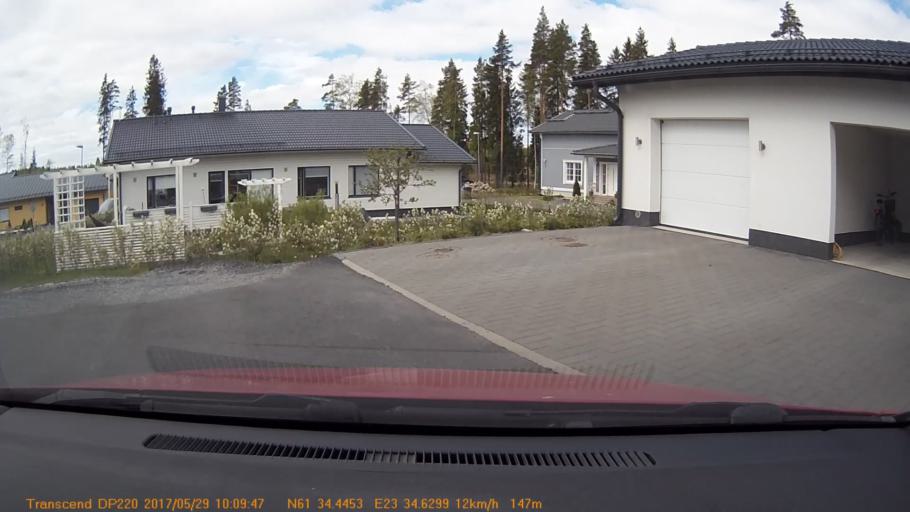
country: FI
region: Pirkanmaa
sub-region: Tampere
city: Yloejaervi
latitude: 61.5741
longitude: 23.5776
